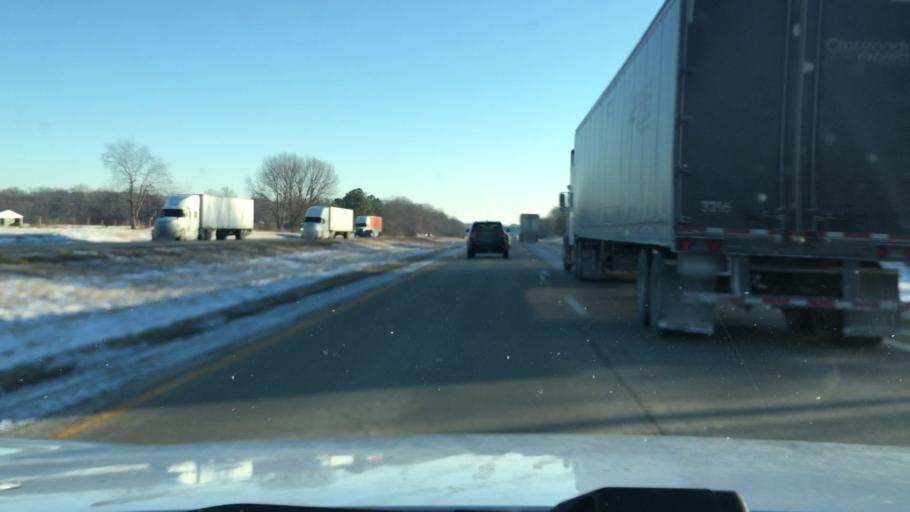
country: US
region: Illinois
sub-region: Effingham County
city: Effingham
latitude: 39.0860
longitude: -88.6097
